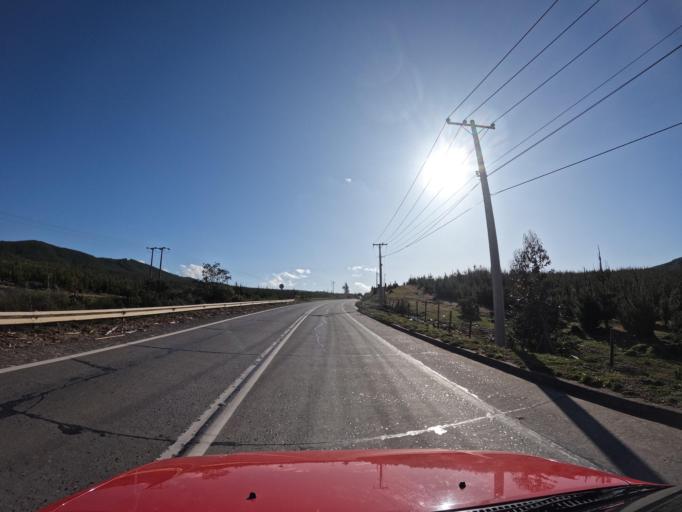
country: CL
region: Maule
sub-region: Provincia de Talca
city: Constitucion
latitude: -35.4465
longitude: -72.3129
